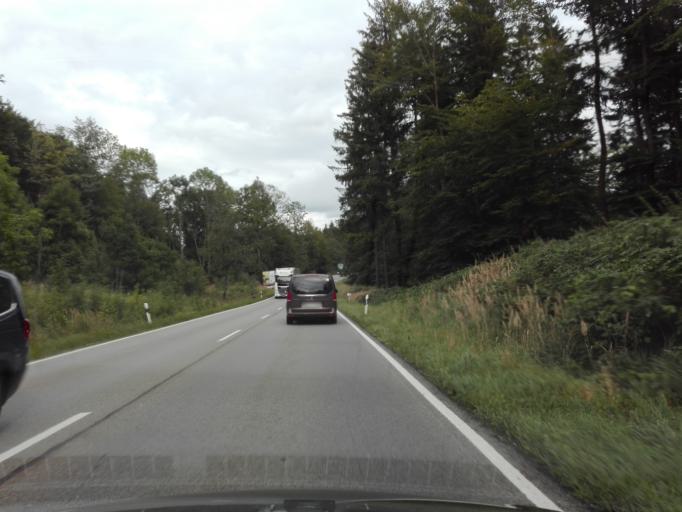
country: DE
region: Bavaria
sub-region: Upper Bavaria
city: Maitenbeth
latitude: 48.1424
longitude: 12.0580
